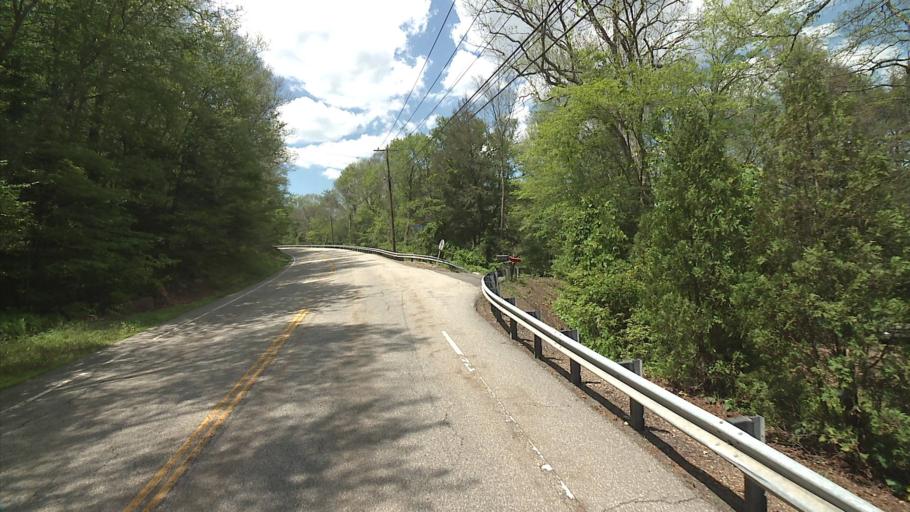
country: US
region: Connecticut
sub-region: Middlesex County
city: Moodus
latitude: 41.5192
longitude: -72.5026
